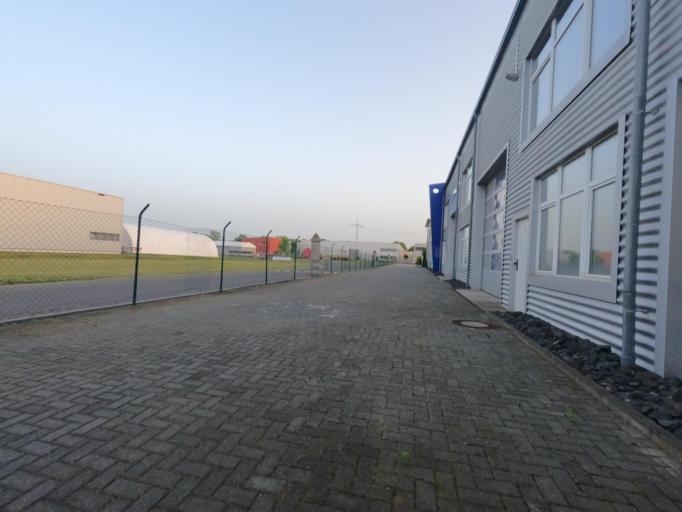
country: DE
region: North Rhine-Westphalia
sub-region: Regierungsbezirk Koln
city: Wassenberg
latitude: 51.0495
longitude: 6.1571
